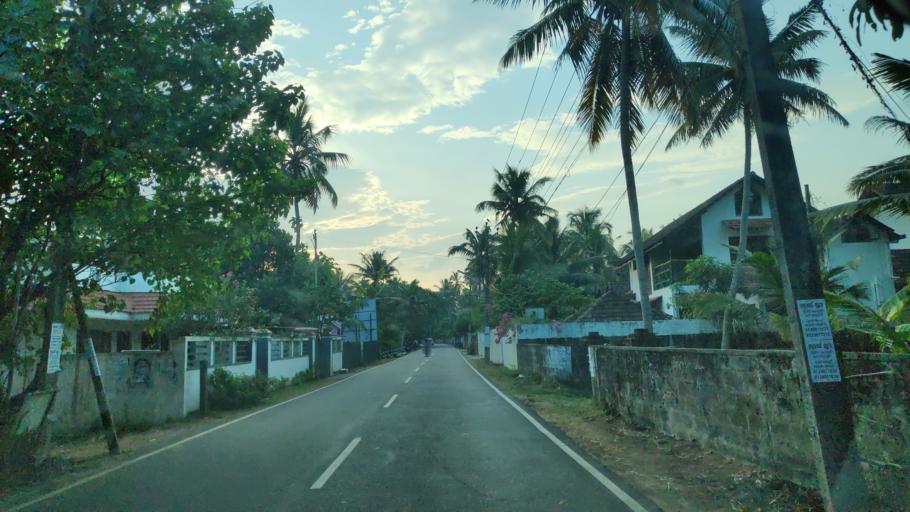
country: IN
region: Kerala
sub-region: Alappuzha
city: Shertallai
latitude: 9.6785
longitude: 76.3880
